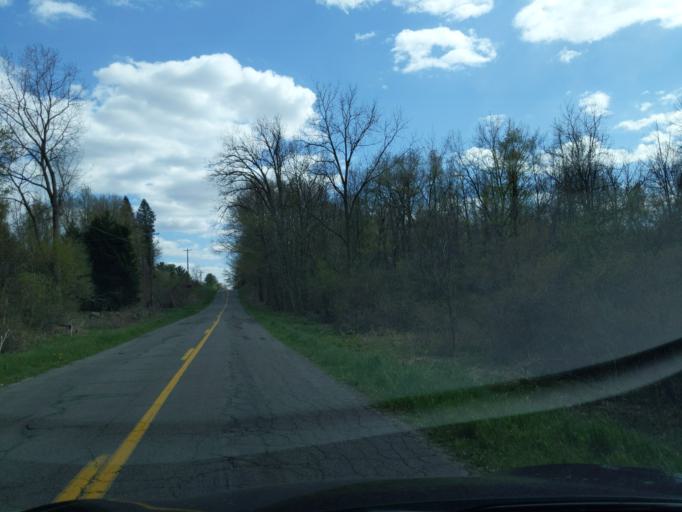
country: US
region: Michigan
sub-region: Ingham County
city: Leslie
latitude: 42.4308
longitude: -84.5409
